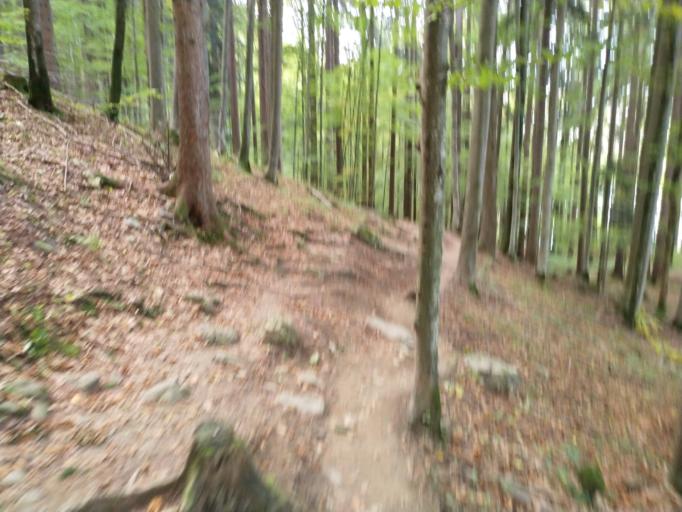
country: AT
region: Tyrol
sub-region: Politischer Bezirk Reutte
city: Vils
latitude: 47.5663
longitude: 10.6364
